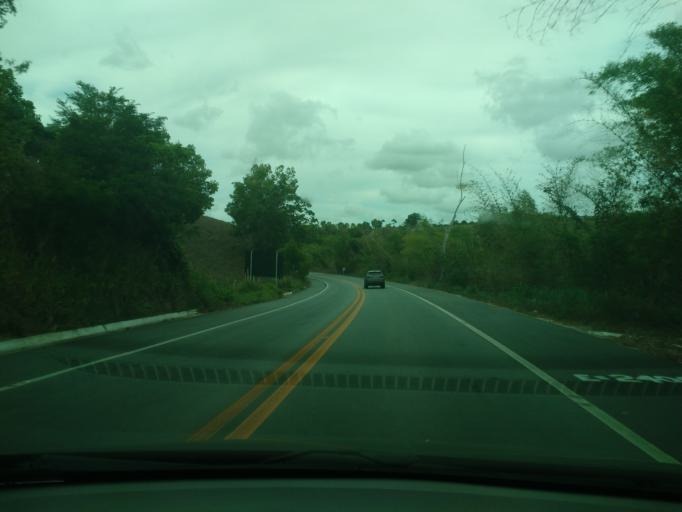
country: BR
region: Alagoas
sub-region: Murici
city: Murici
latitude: -9.2475
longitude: -35.9987
